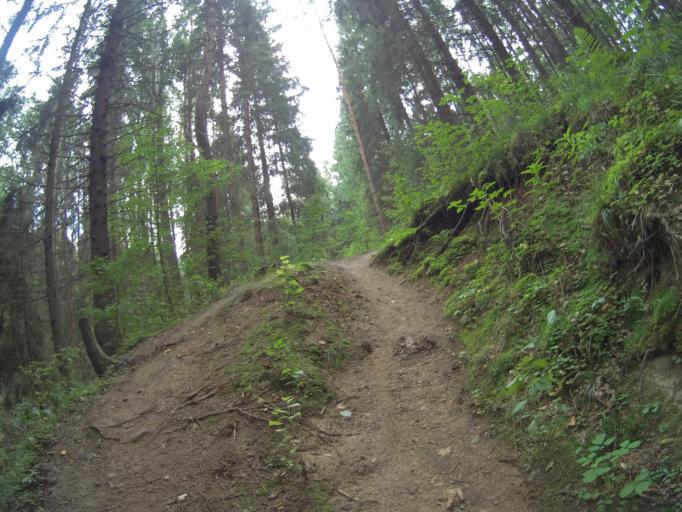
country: RU
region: Vladimir
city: Raduzhnyy
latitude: 56.0011
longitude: 40.3171
